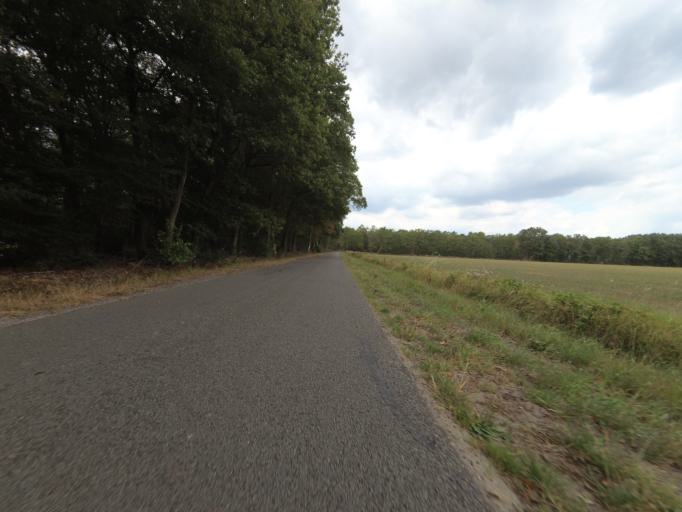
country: NL
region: Overijssel
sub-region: Gemeente Haaksbergen
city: Haaksbergen
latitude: 52.1408
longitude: 6.7841
